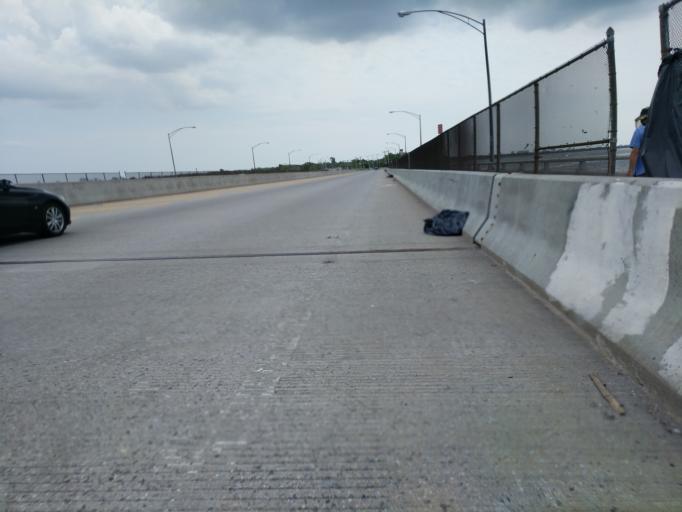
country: US
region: New York
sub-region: Queens County
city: Borough of Queens
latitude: 40.6412
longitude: -73.8343
